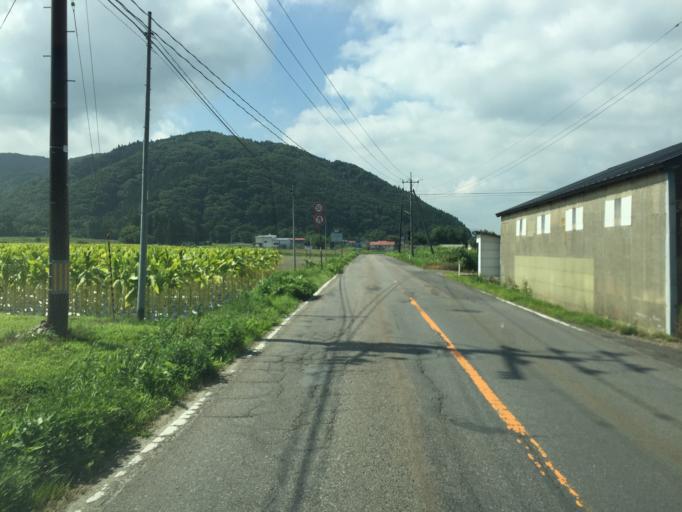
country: JP
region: Fukushima
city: Inawashiro
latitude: 37.4437
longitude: 140.1521
